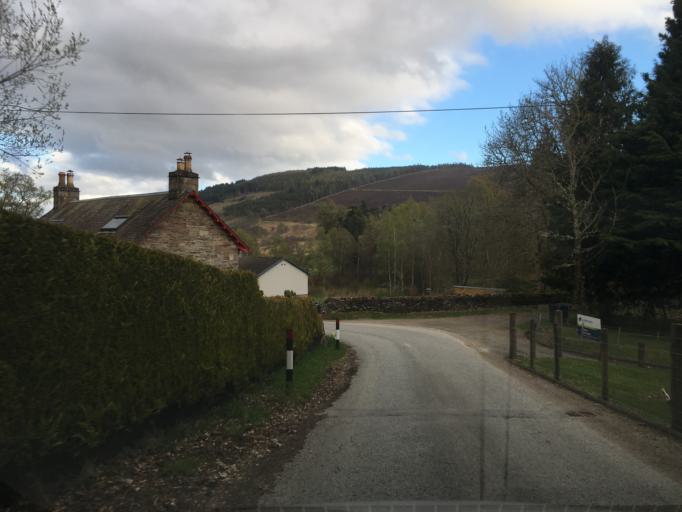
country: GB
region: Scotland
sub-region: Perth and Kinross
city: Aberfeldy
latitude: 56.7572
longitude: -4.0872
